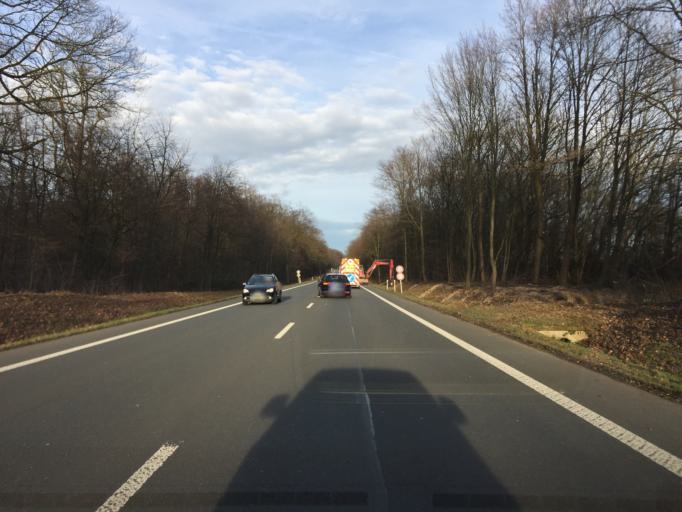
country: DE
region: North Rhine-Westphalia
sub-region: Regierungsbezirk Detmold
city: Petershagen
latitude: 52.3476
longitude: 8.9465
